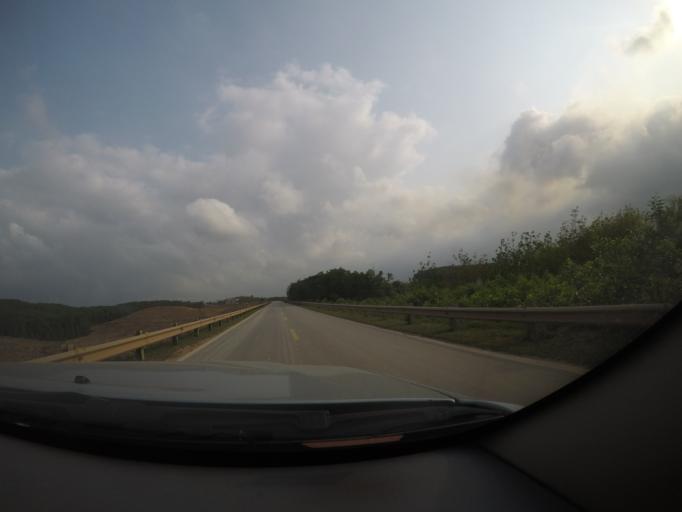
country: VN
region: Quang Binh
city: Kien Giang
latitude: 17.1017
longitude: 106.8465
